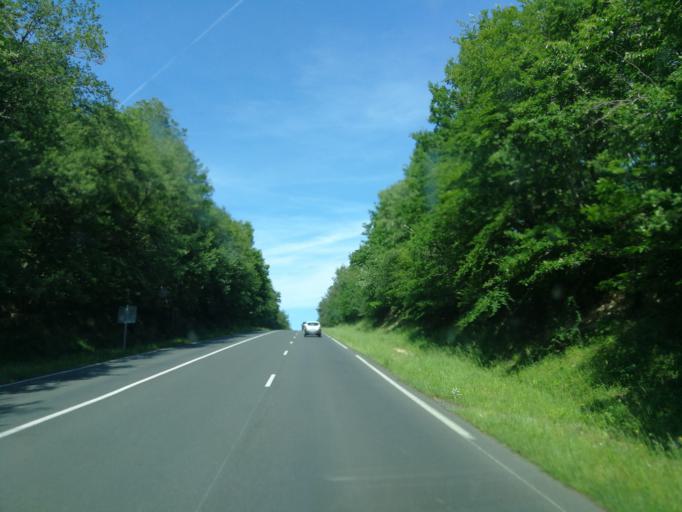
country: FR
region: Centre
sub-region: Departement d'Indre-et-Loire
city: Huismes
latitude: 47.2009
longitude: 0.3217
